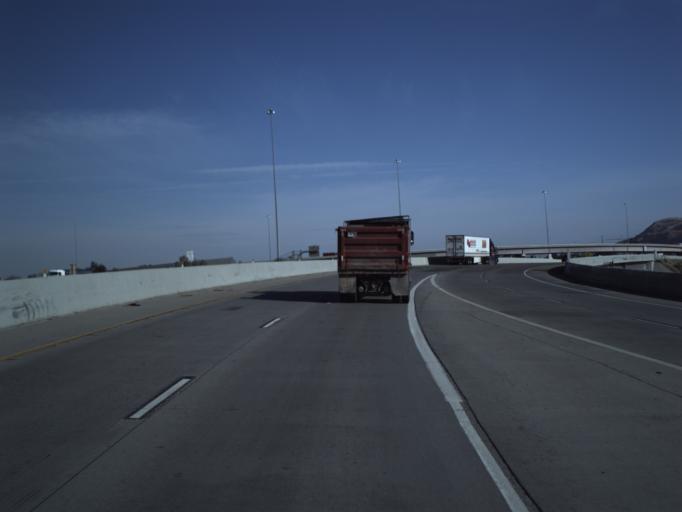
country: US
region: Utah
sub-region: Salt Lake County
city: Salt Lake City
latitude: 40.7593
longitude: -111.9133
